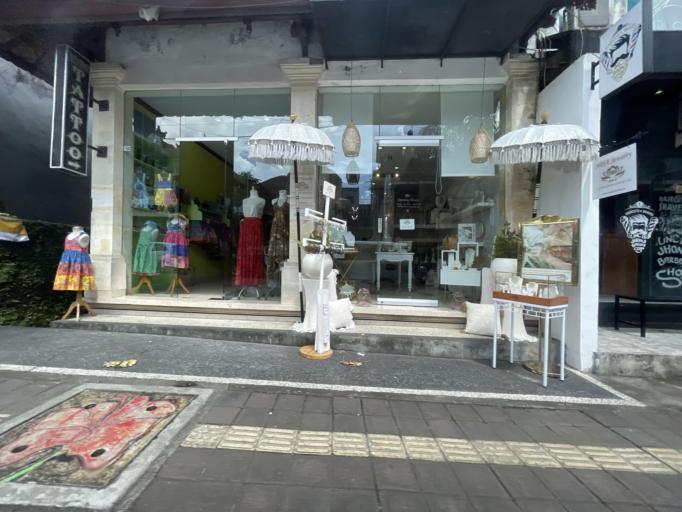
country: ID
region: Bali
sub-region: Kabupaten Gianyar
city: Ubud
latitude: -8.5123
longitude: 115.2611
